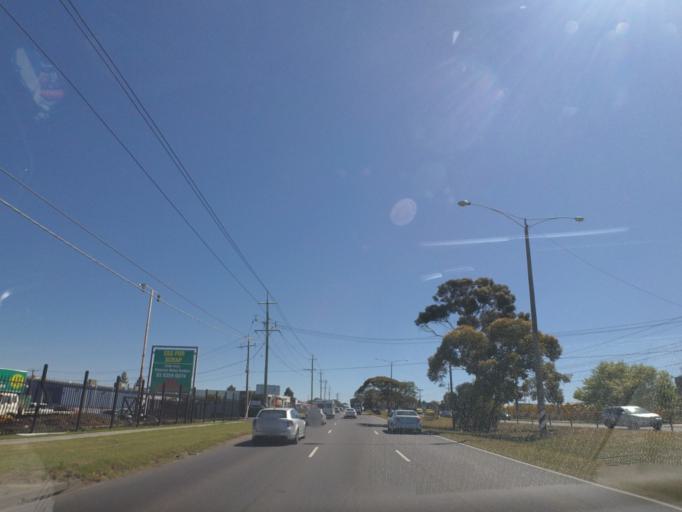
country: AU
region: Victoria
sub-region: Hume
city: Campbellfield
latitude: -37.6820
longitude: 144.9569
